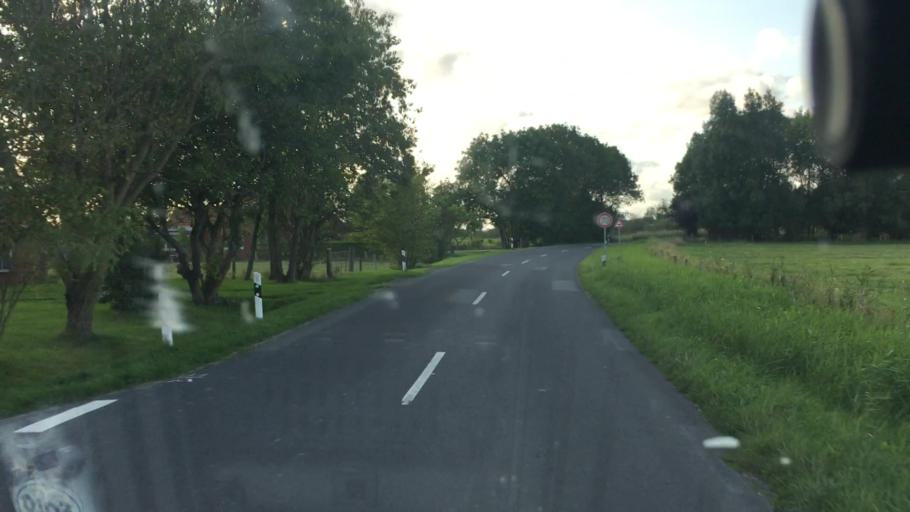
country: DE
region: Lower Saxony
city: Werdum
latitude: 53.6753
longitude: 7.7182
